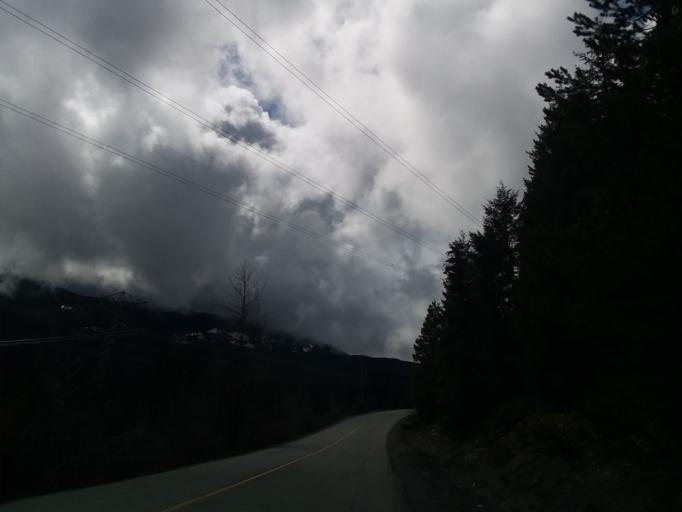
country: CA
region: British Columbia
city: Whistler
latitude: 50.1001
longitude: -123.0006
